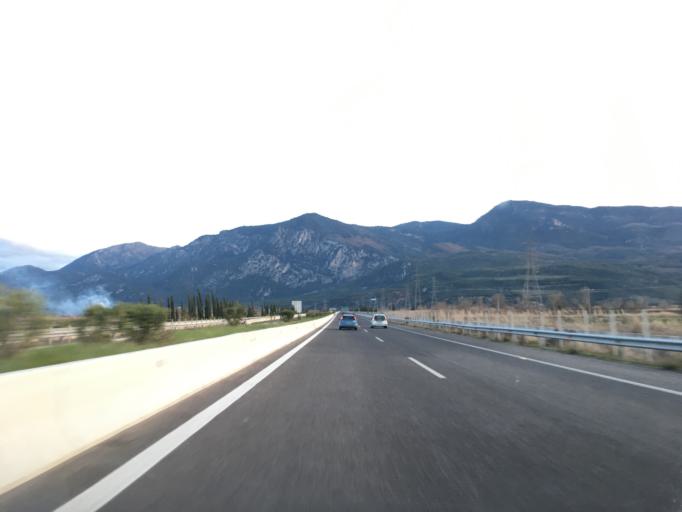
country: GR
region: Central Greece
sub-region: Nomos Fthiotidos
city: Anthili
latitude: 38.8244
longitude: 22.4871
